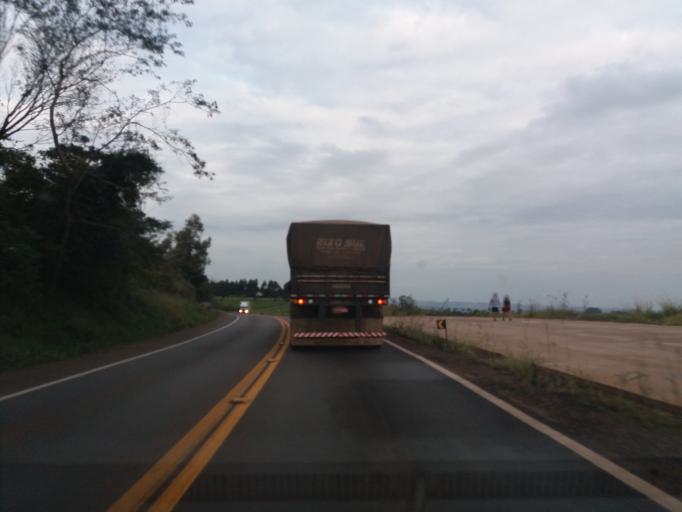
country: BR
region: Parana
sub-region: Cascavel
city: Cascavel
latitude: -25.2421
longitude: -53.5855
